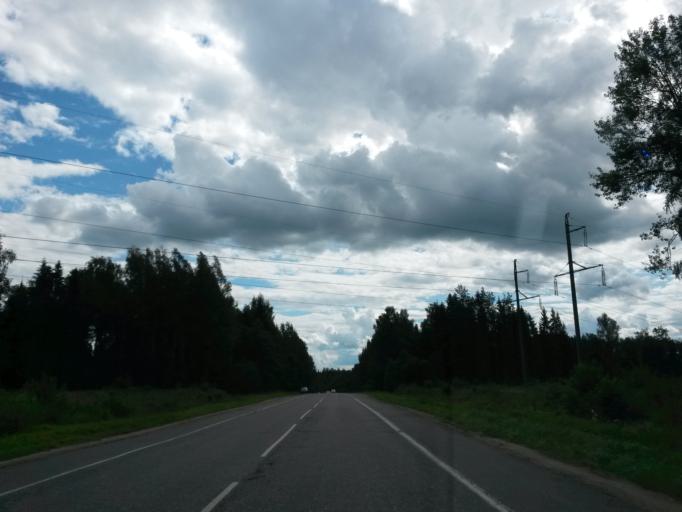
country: RU
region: Ivanovo
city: Pistsovo
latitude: 57.1069
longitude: 40.6514
